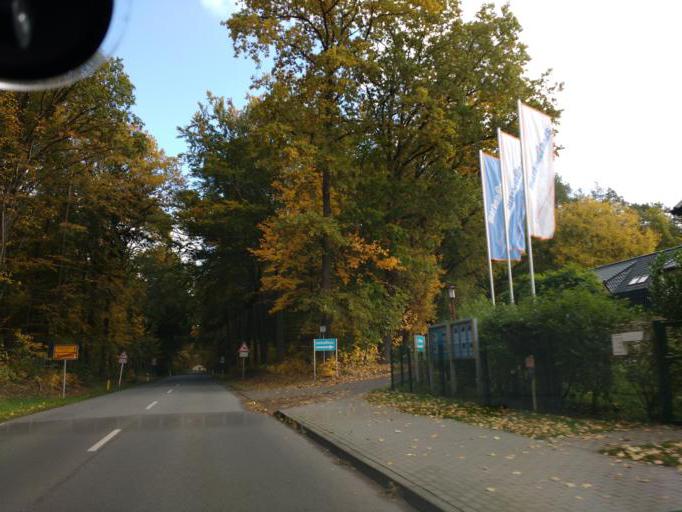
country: DE
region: Brandenburg
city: Petershagen
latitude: 52.5587
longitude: 13.7776
